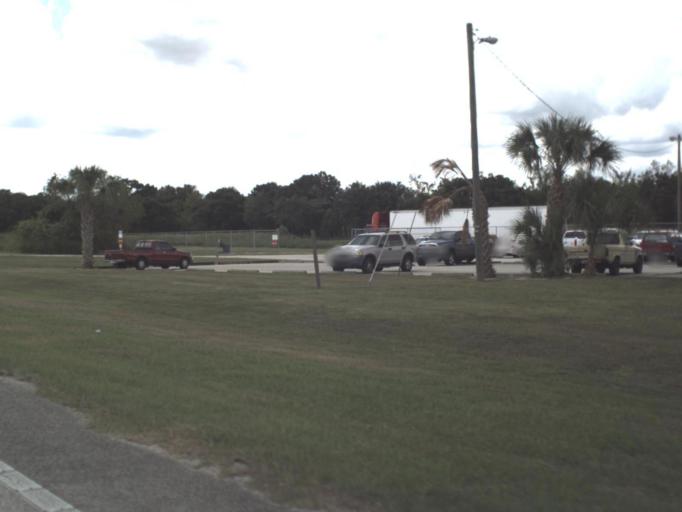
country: US
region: Florida
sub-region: Polk County
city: Mulberry
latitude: 27.8950
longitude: -81.9857
